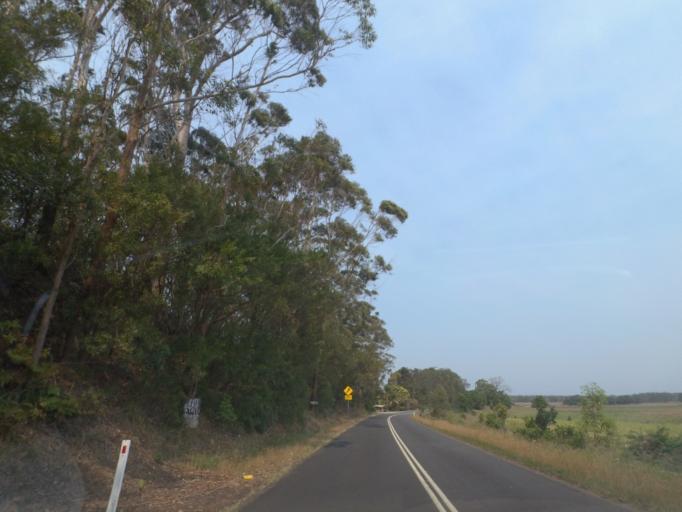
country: AU
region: New South Wales
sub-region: Tweed
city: Burringbar
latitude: -28.4534
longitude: 153.5334
